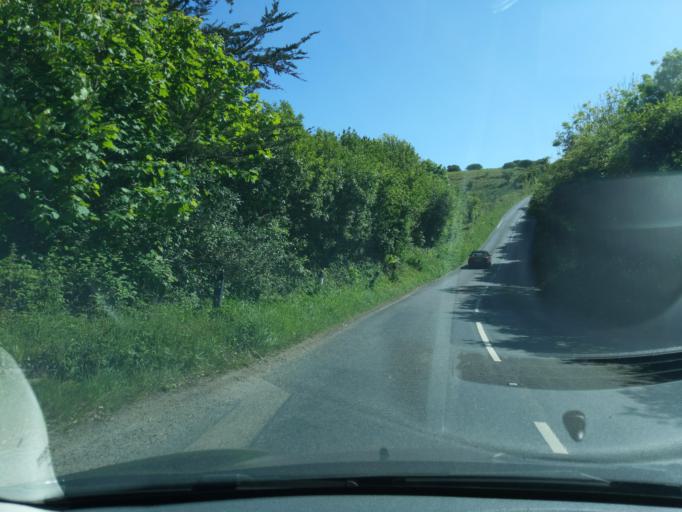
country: GB
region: England
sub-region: Cornwall
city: St. Buryan
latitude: 50.0904
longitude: -5.5988
